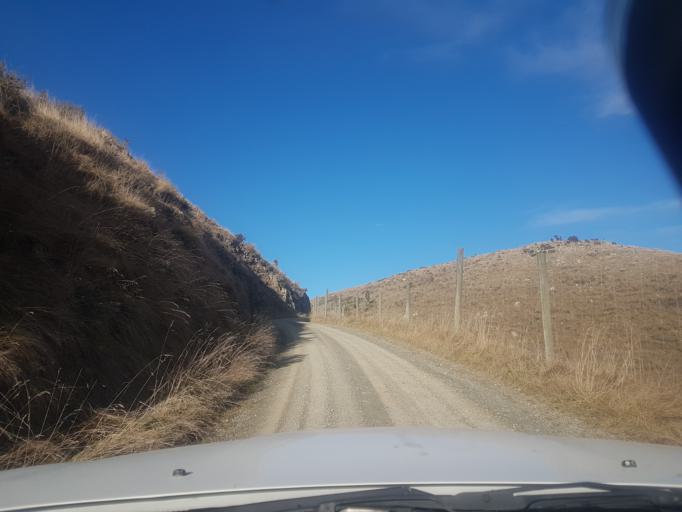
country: NZ
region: Canterbury
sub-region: Timaru District
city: Pleasant Point
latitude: -44.1738
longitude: 170.8842
